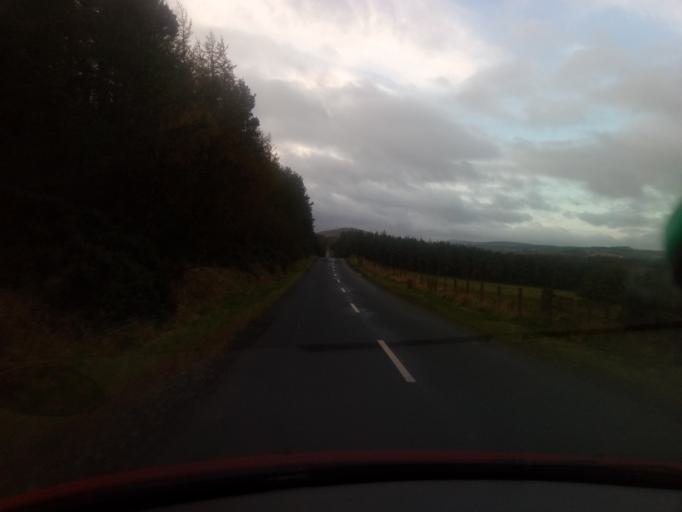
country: GB
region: Scotland
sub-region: The Scottish Borders
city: Jedburgh
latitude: 55.4301
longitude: -2.6106
